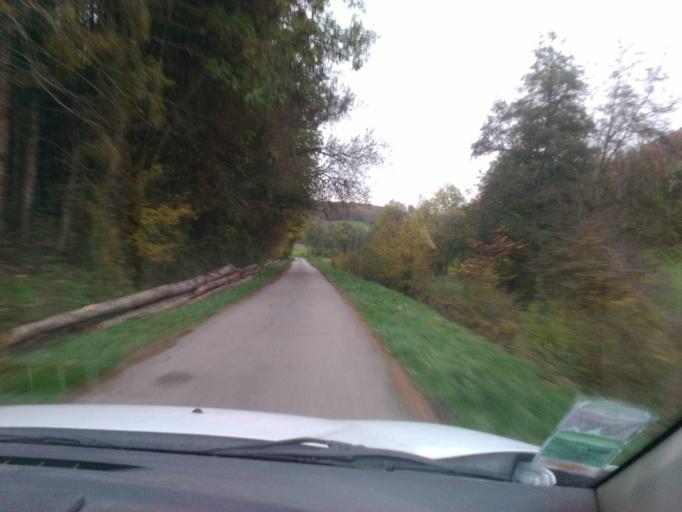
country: FR
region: Lorraine
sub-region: Departement des Vosges
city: Mirecourt
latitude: 48.2776
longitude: 6.2199
